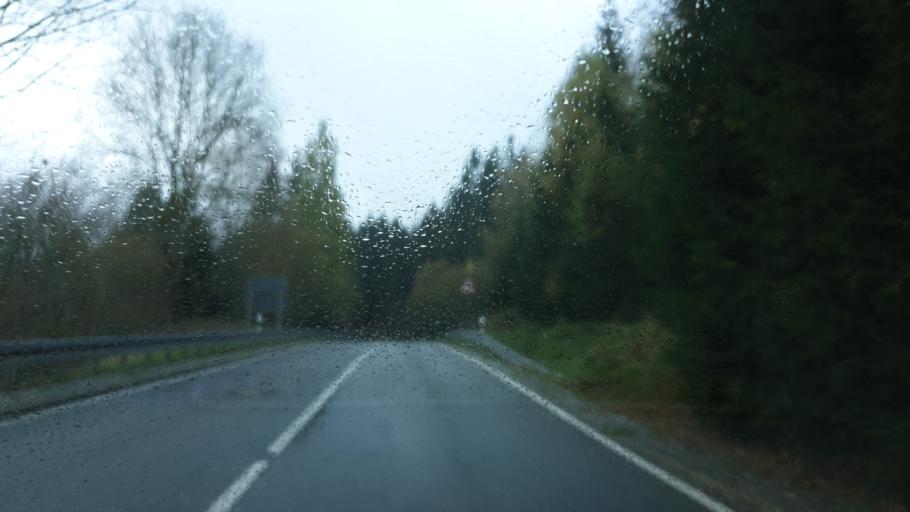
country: DE
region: Saxony
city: Schoenheide
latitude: 50.4731
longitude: 12.5144
